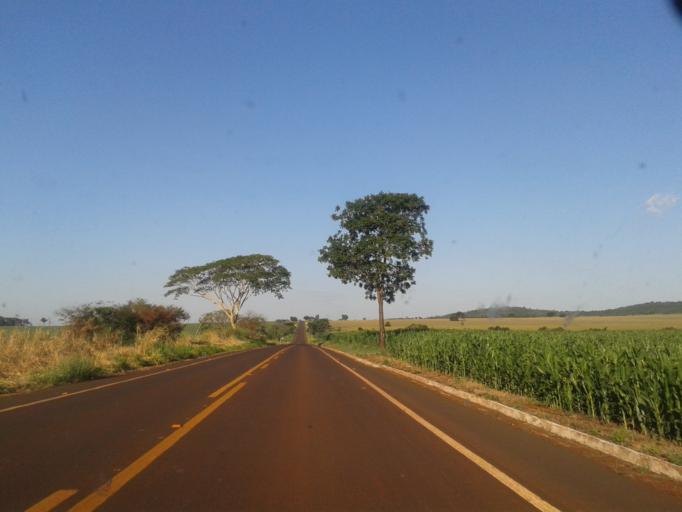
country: BR
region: Minas Gerais
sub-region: Capinopolis
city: Capinopolis
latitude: -18.7121
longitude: -49.8205
